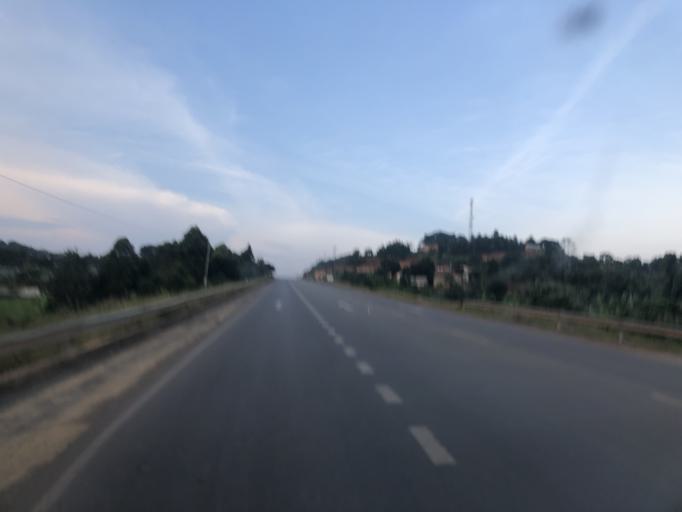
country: UG
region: Central Region
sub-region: Mpigi District
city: Mpigi
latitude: 0.2151
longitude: 32.3270
